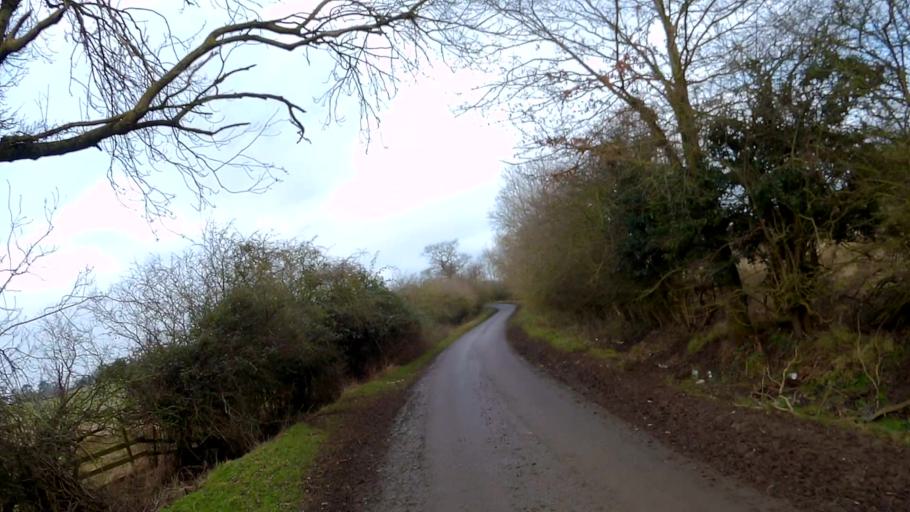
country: GB
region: England
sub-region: Lincolnshire
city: Bourne
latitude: 52.8139
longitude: -0.4364
